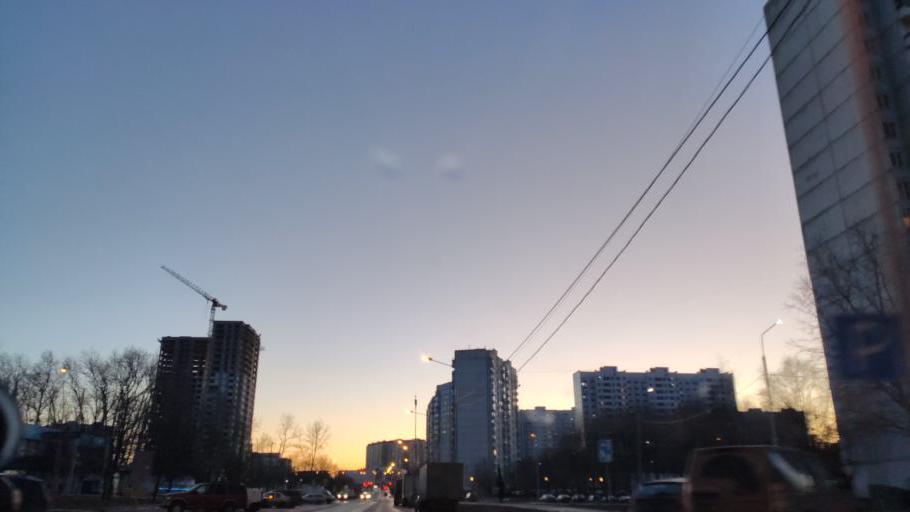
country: RU
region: Moscow
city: Solntsevo
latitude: 55.6473
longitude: 37.4074
